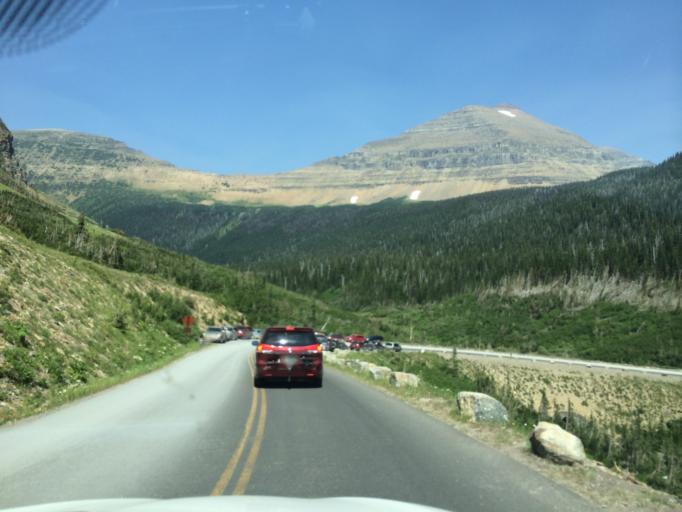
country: US
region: Montana
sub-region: Flathead County
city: Columbia Falls
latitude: 48.7004
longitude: -113.6688
